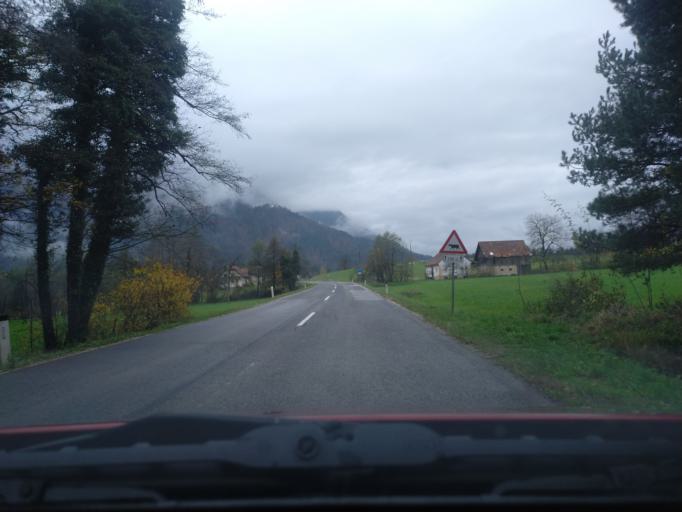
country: SI
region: Gornji Grad
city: Gornji Grad
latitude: 46.3048
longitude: 14.8353
